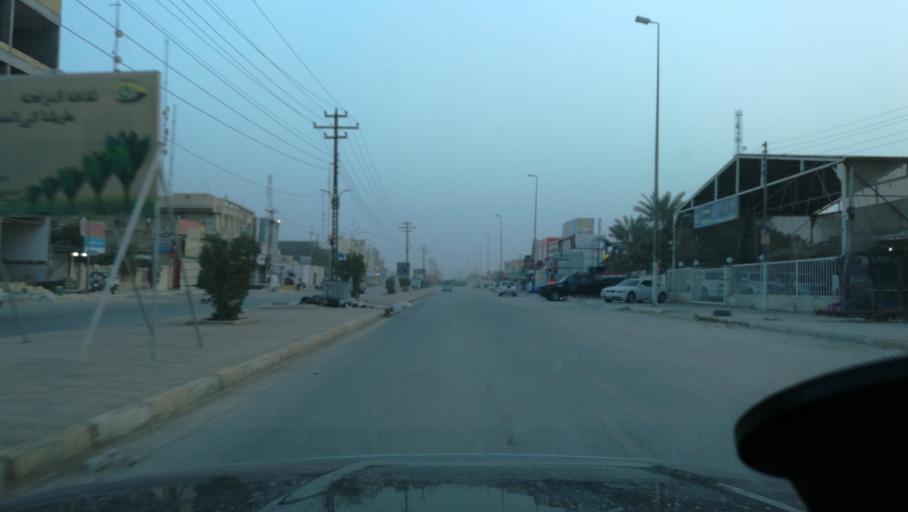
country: IQ
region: Dhi Qar
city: An Nasiriyah
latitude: 31.0348
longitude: 46.2375
